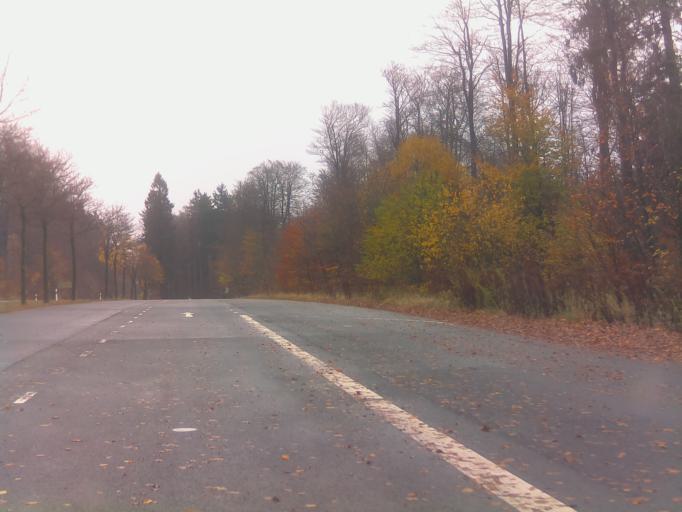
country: DE
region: Hesse
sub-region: Regierungsbezirk Giessen
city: Ulrichstein
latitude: 50.5151
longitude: 9.2390
